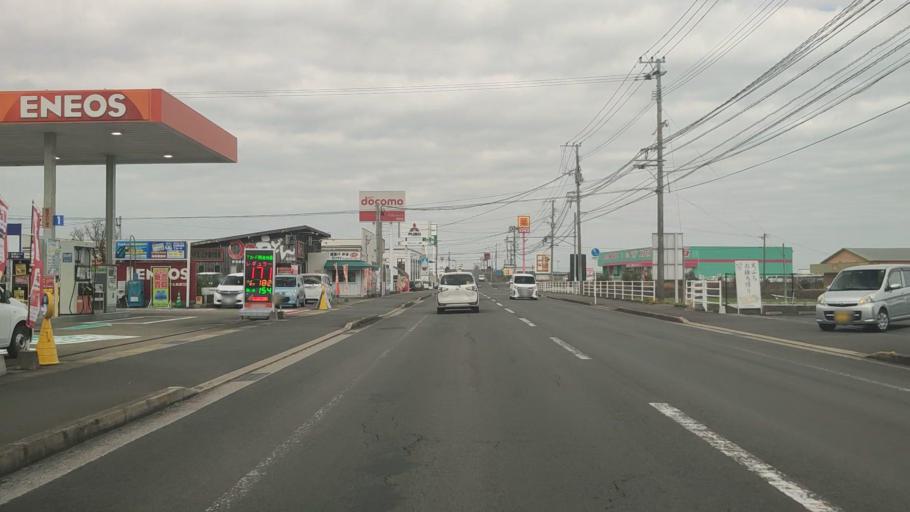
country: JP
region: Nagasaki
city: Shimabara
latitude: 32.8052
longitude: 130.3622
